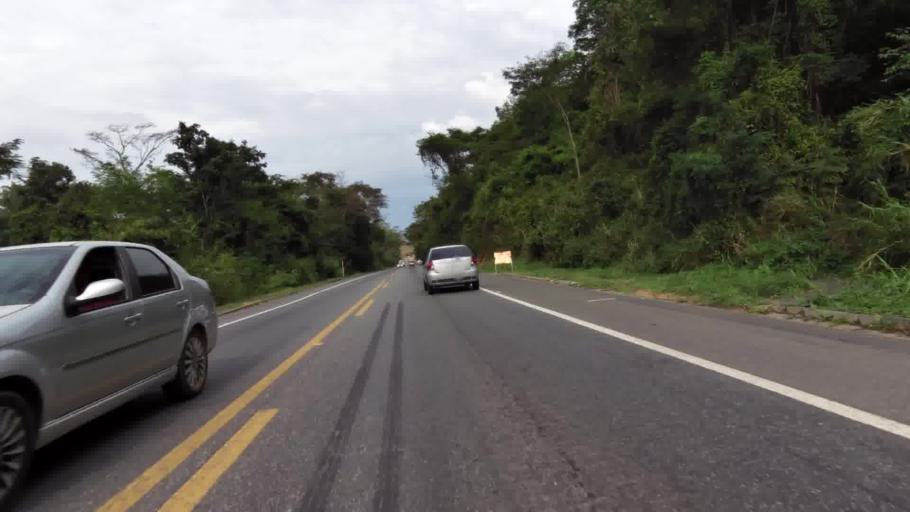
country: BR
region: Espirito Santo
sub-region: Alfredo Chaves
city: Alfredo Chaves
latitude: -20.7114
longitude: -40.7232
